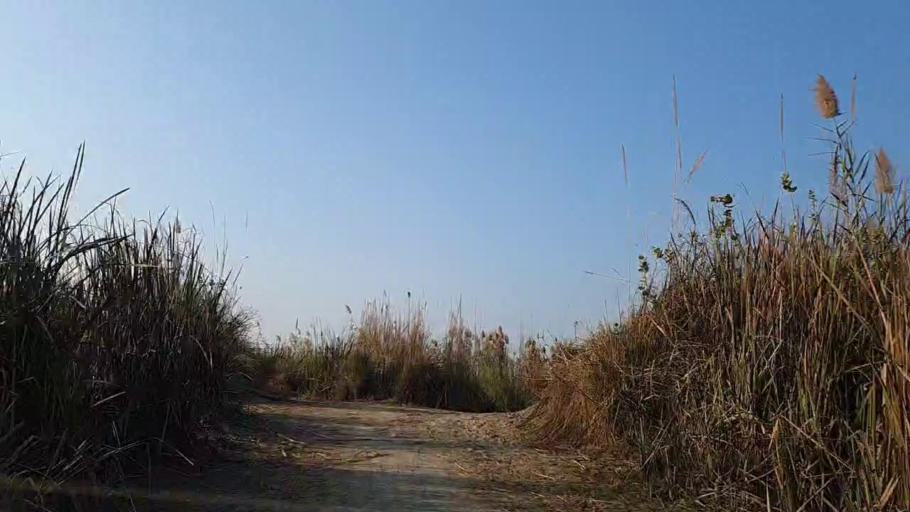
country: PK
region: Sindh
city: Sakrand
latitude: 26.0933
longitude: 68.3795
